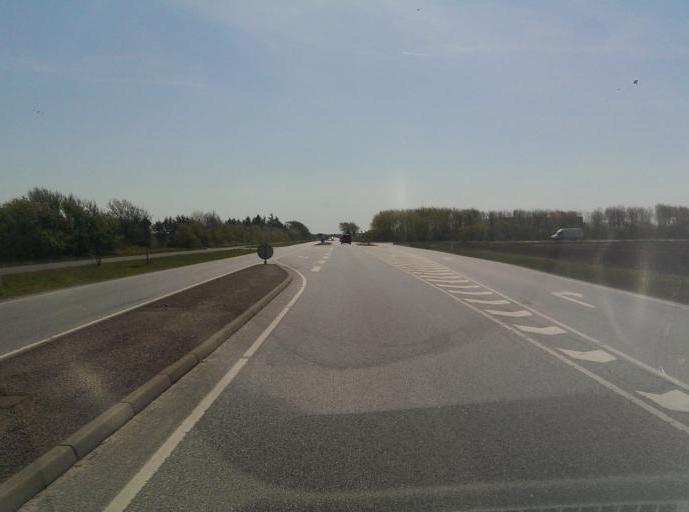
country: DK
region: South Denmark
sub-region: Esbjerg Kommune
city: Ribe
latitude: 55.3629
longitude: 8.7705
